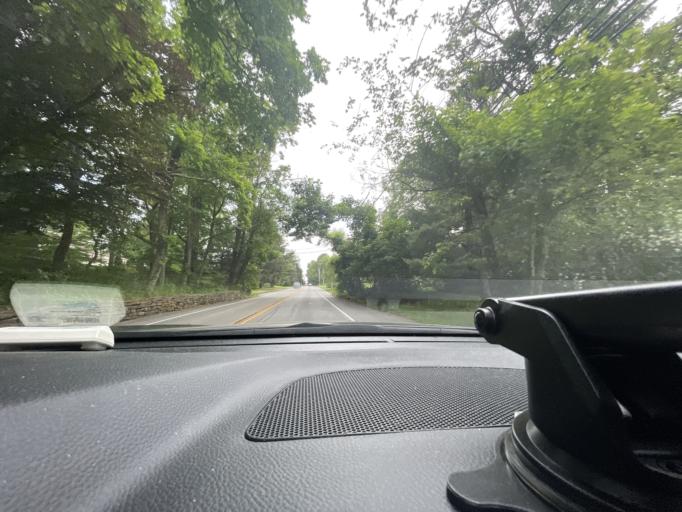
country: US
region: Pennsylvania
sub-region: Montgomery County
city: Blue Bell
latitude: 40.1602
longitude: -75.2591
